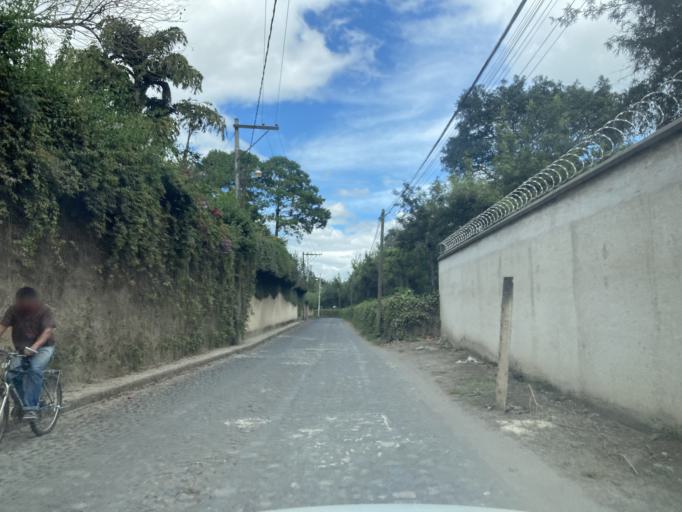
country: GT
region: Sacatepequez
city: Antigua Guatemala
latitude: 14.5472
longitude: -90.7336
